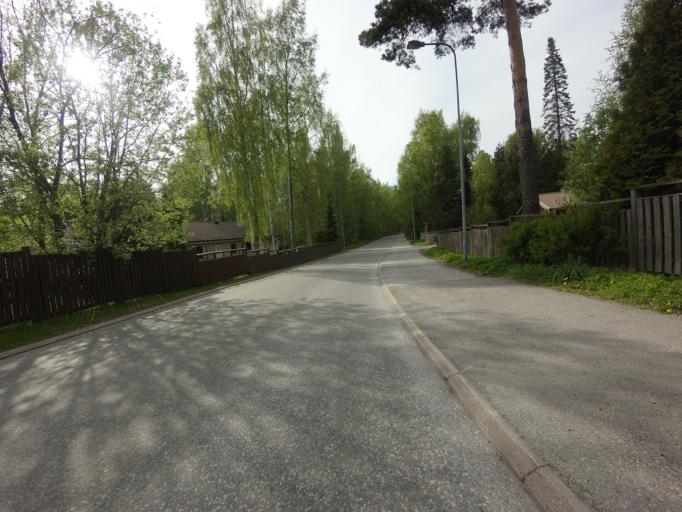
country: FI
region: Uusimaa
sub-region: Helsinki
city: Koukkuniemi
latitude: 60.1496
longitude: 24.7022
